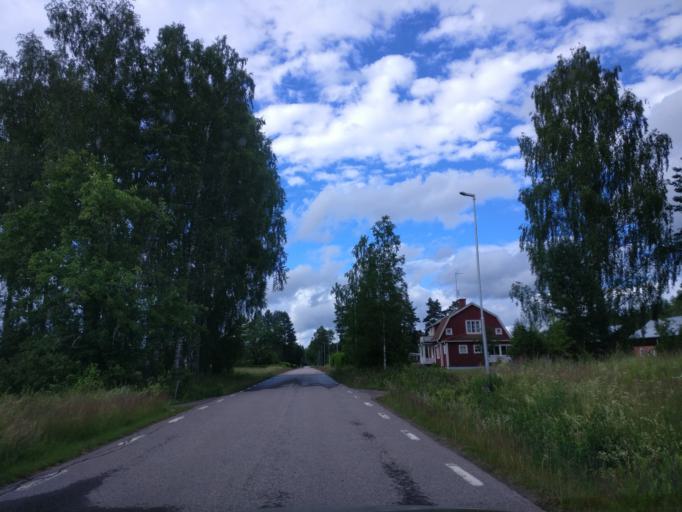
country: SE
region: Vaermland
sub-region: Munkfors Kommun
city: Munkfors
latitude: 59.9706
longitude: 13.4869
